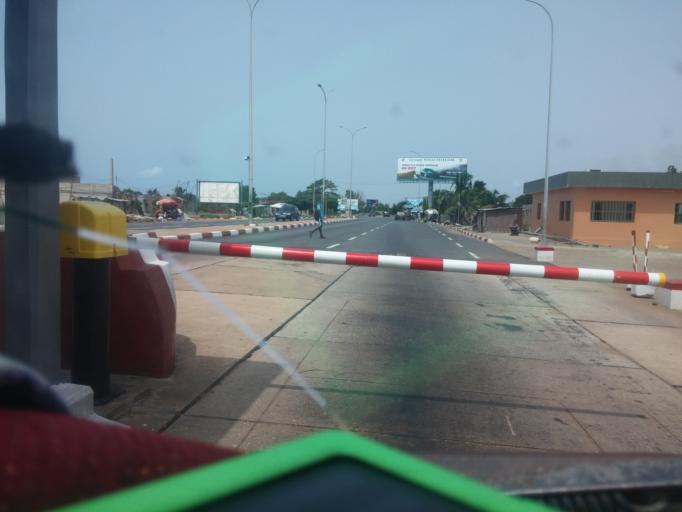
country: TG
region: Maritime
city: Aneho
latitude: 6.2261
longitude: 1.5595
